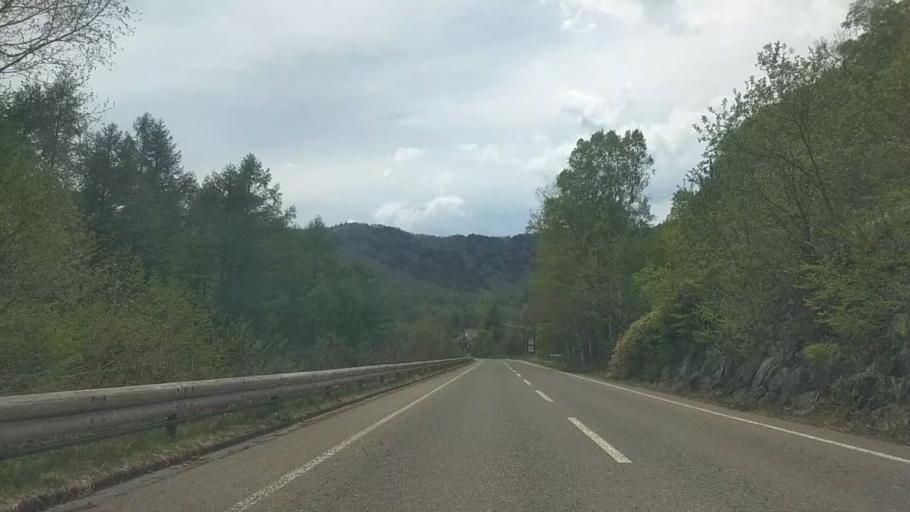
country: JP
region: Nagano
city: Saku
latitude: 36.0736
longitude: 138.3818
